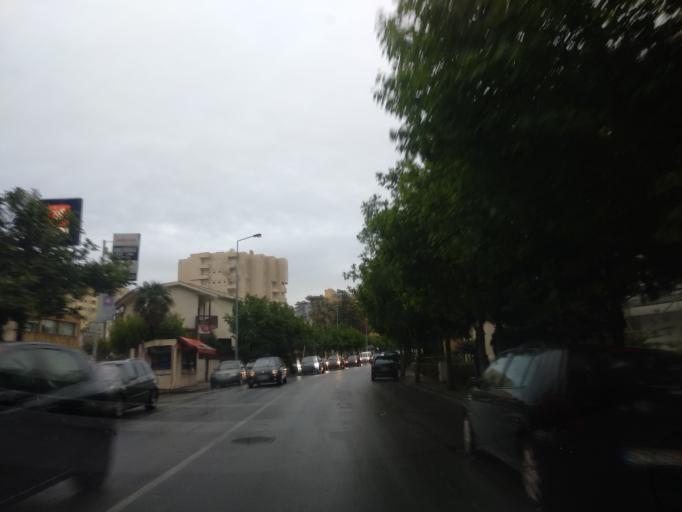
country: PT
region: Porto
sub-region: Gondomar
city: Rio Tinto
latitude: 41.1768
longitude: -8.5588
